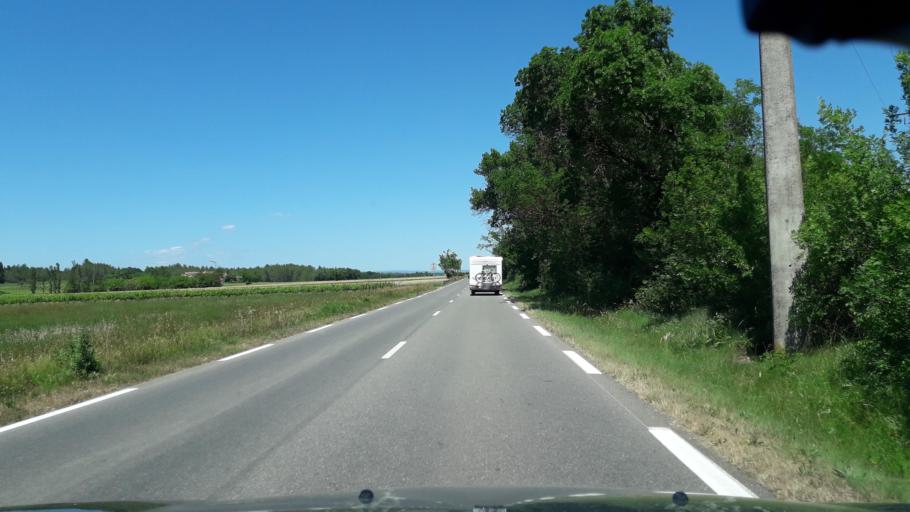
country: FR
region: Rhone-Alpes
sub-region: Departement de l'Ardeche
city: Rosieres
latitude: 44.3999
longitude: 4.2700
